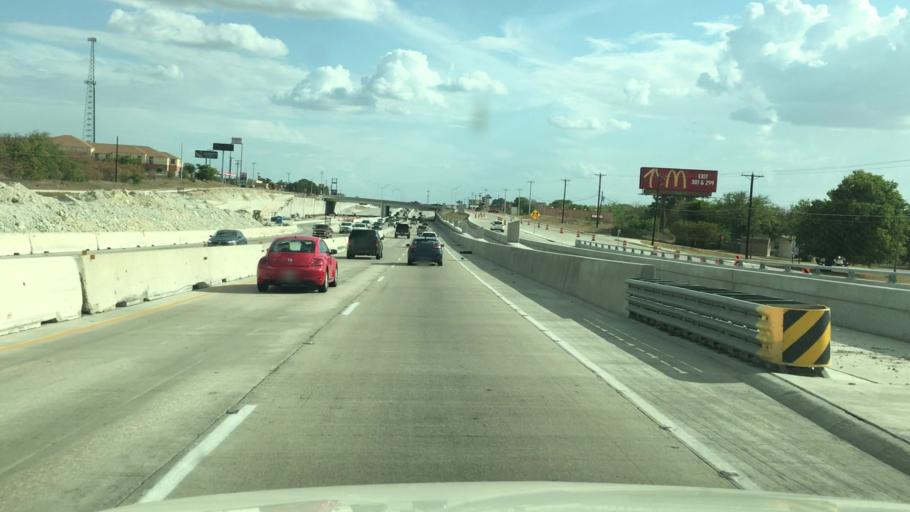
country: US
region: Texas
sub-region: Bell County
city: Temple
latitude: 31.1184
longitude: -97.3539
